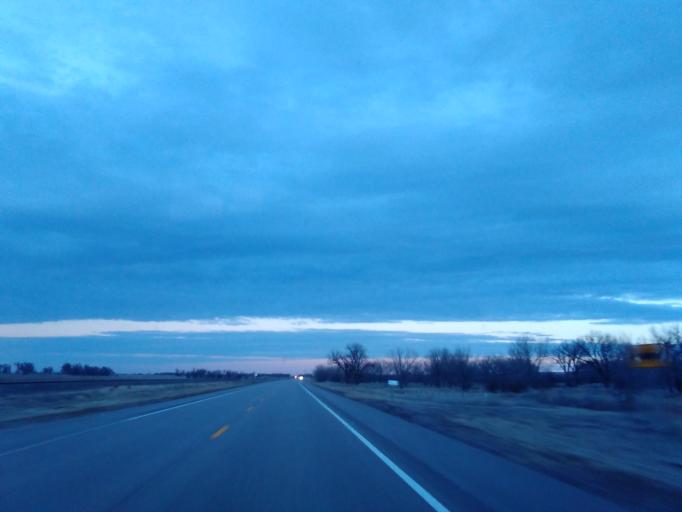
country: US
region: Nebraska
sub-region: Garden County
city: Oshkosh
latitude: 41.3644
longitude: -102.2272
